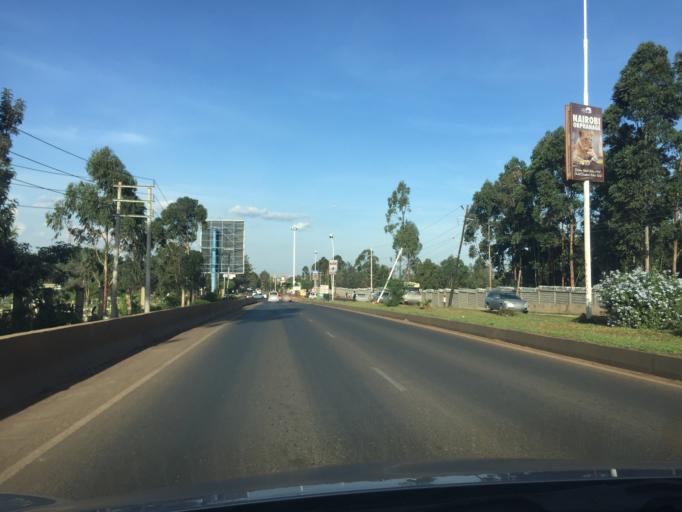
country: KE
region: Nairobi Area
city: Nairobi
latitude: -1.3336
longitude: 36.7803
